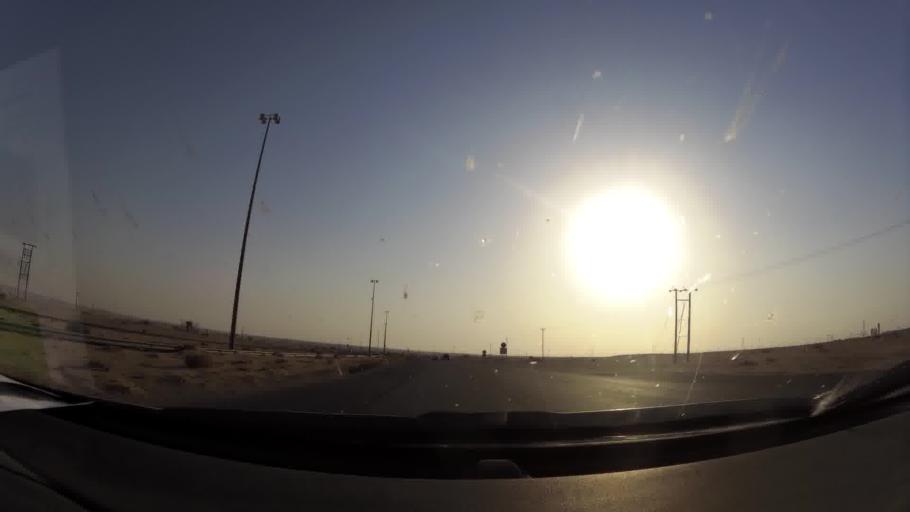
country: KW
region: Muhafazat al Jahra'
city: Al Jahra'
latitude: 29.4422
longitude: 47.6400
